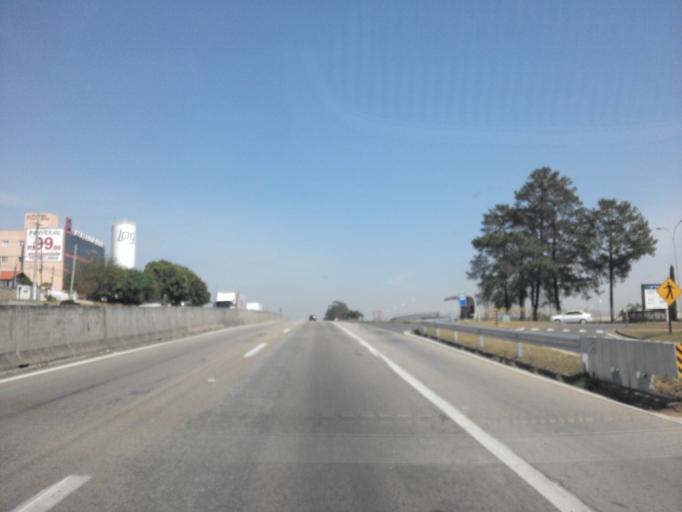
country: BR
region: Sao Paulo
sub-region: Hortolandia
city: Hortolandia
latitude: -22.9000
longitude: -47.1975
